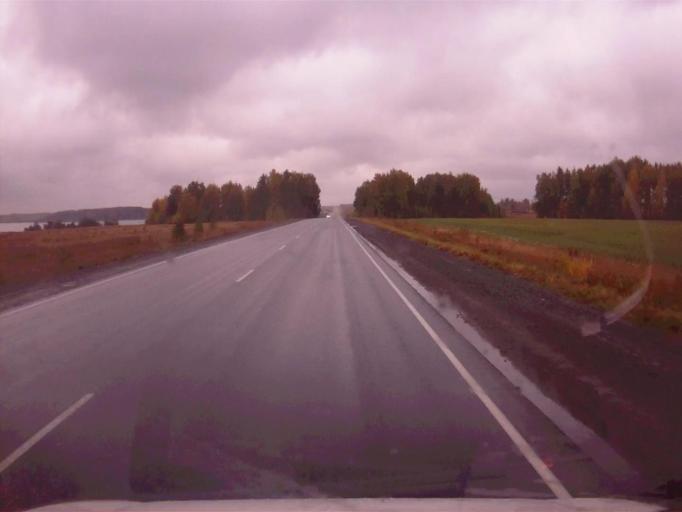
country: RU
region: Chelyabinsk
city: Roshchino
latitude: 55.3858
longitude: 61.1320
